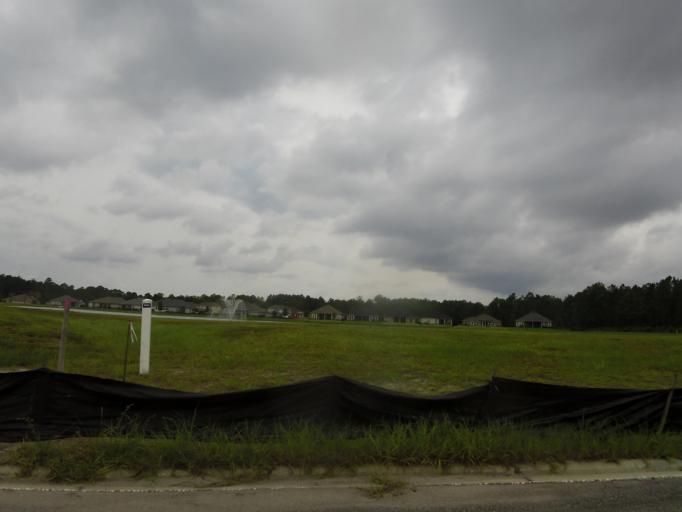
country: US
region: Florida
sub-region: Clay County
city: Middleburg
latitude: 30.1104
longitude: -81.8596
